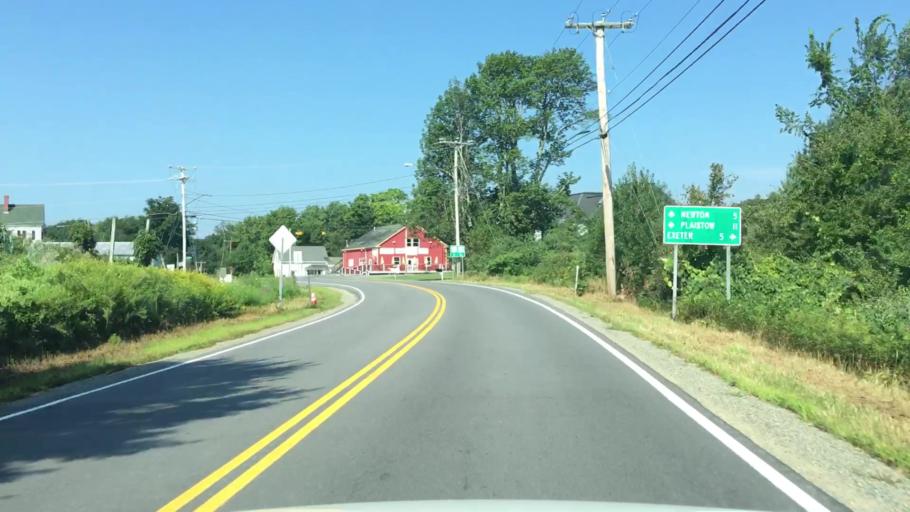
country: US
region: New Hampshire
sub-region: Rockingham County
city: East Kingston
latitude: 42.9214
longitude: -70.9903
